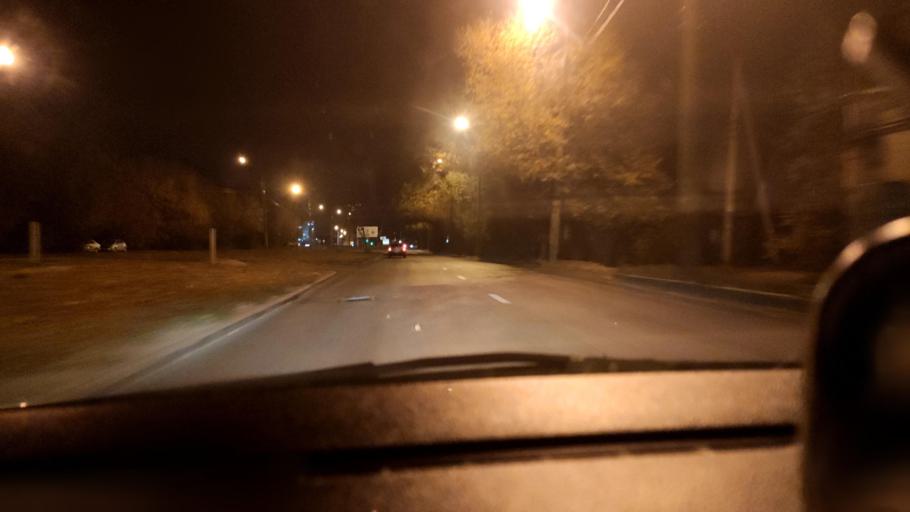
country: RU
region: Voronezj
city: Voronezh
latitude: 51.6370
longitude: 39.1680
